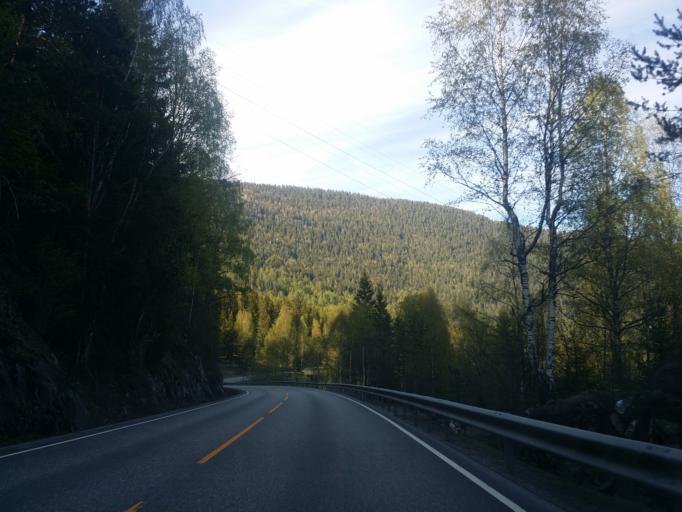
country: NO
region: Telemark
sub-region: Hjartdal
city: Sauland
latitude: 59.6137
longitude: 8.7890
